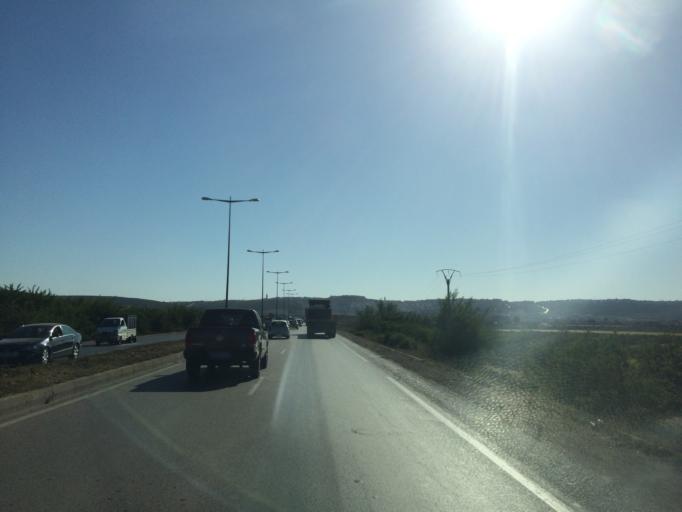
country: MA
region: Rabat-Sale-Zemmour-Zaer
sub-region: Rabat
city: Rabat
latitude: 33.9878
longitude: -6.7837
